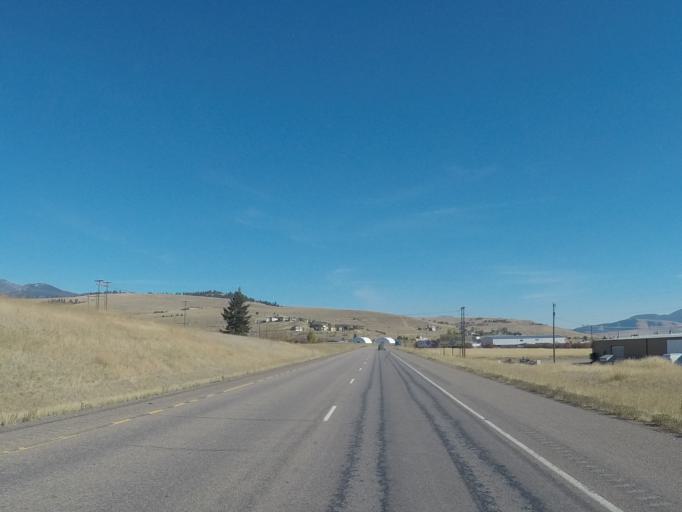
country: US
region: Montana
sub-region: Missoula County
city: Orchard Homes
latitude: 46.9383
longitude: -114.1049
